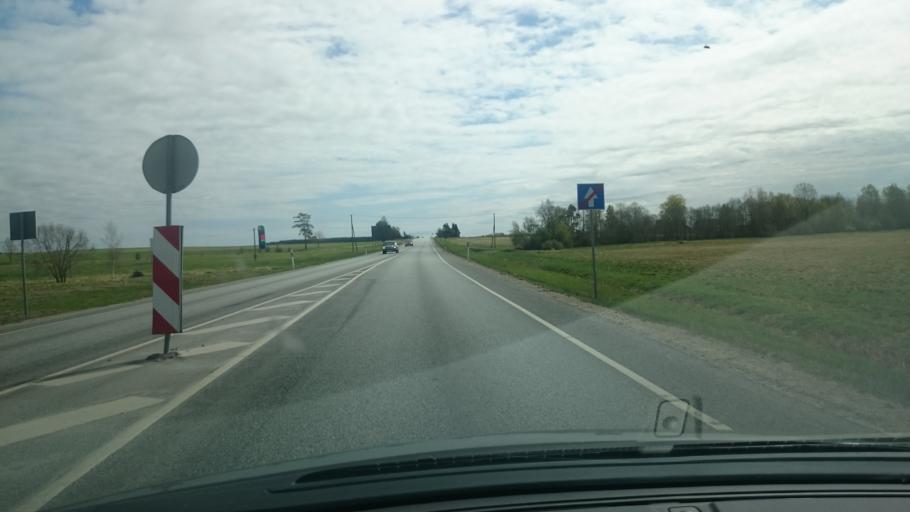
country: EE
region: Laeaene-Virumaa
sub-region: Haljala vald
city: Haljala
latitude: 59.4213
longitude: 26.2934
